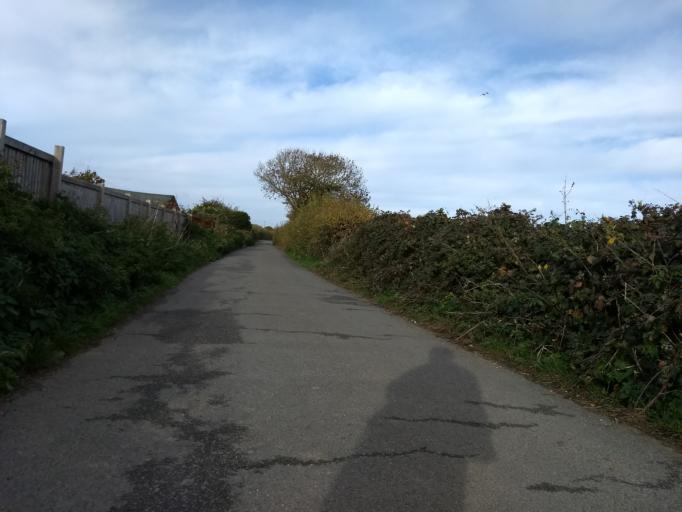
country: GB
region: England
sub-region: Isle of Wight
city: Freshwater
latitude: 50.6869
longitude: -1.5106
